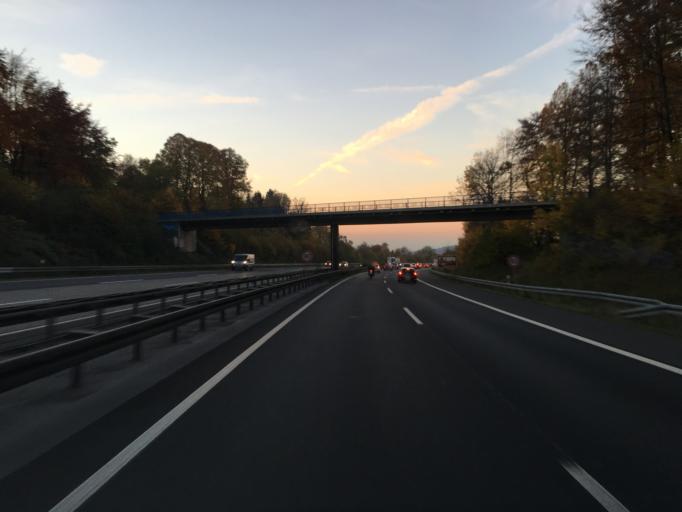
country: DE
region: North Rhine-Westphalia
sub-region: Regierungsbezirk Arnsberg
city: Schalksmuhle
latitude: 51.2919
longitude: 7.5565
